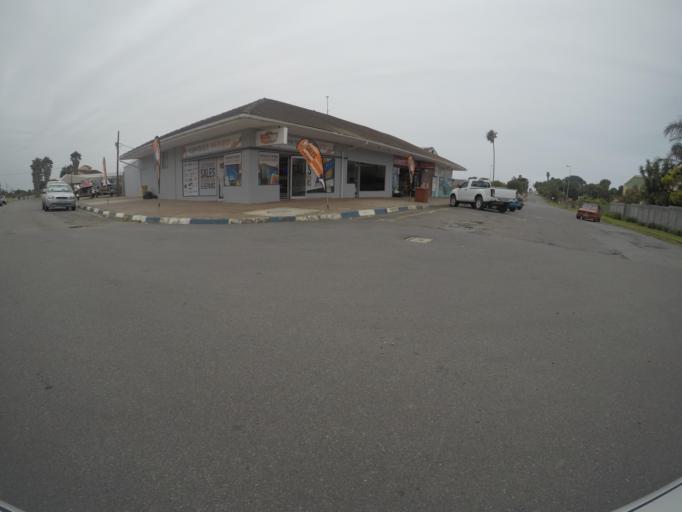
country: ZA
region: Eastern Cape
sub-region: Buffalo City Metropolitan Municipality
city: East London
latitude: -32.9638
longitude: 27.9321
